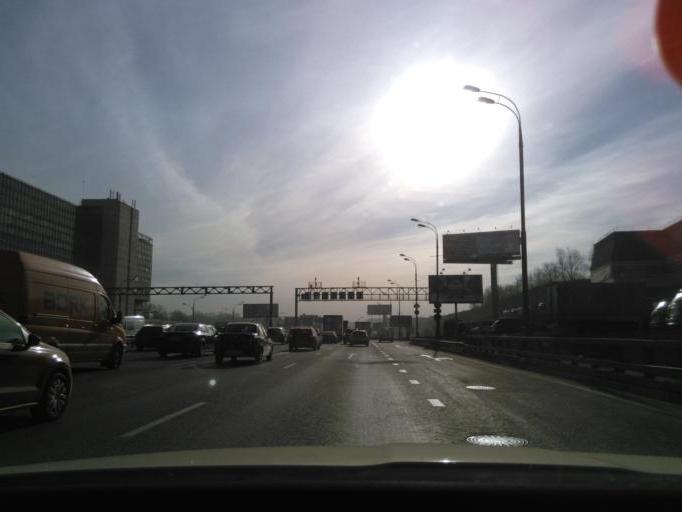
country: RU
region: Moscow
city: Novyye Cheremushki
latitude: 55.7046
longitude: 37.5959
